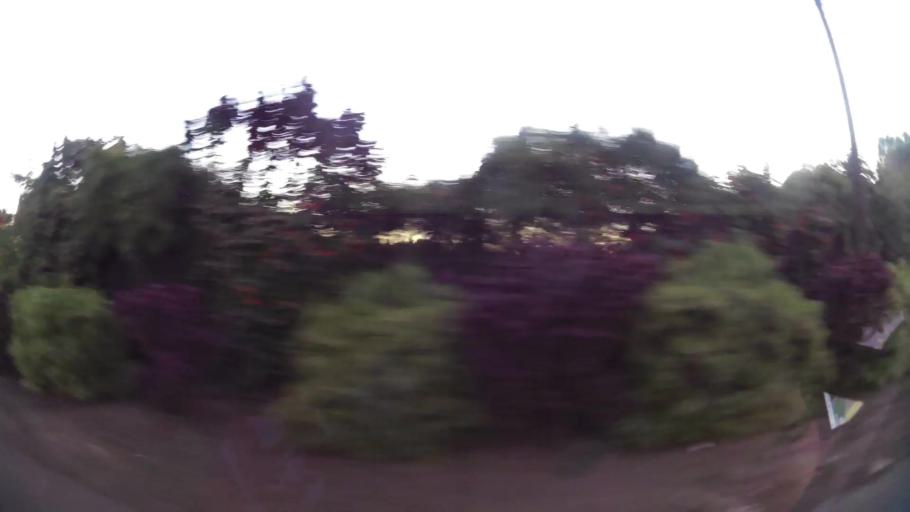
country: MU
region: Moka
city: Moka
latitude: -20.2220
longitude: 57.5010
